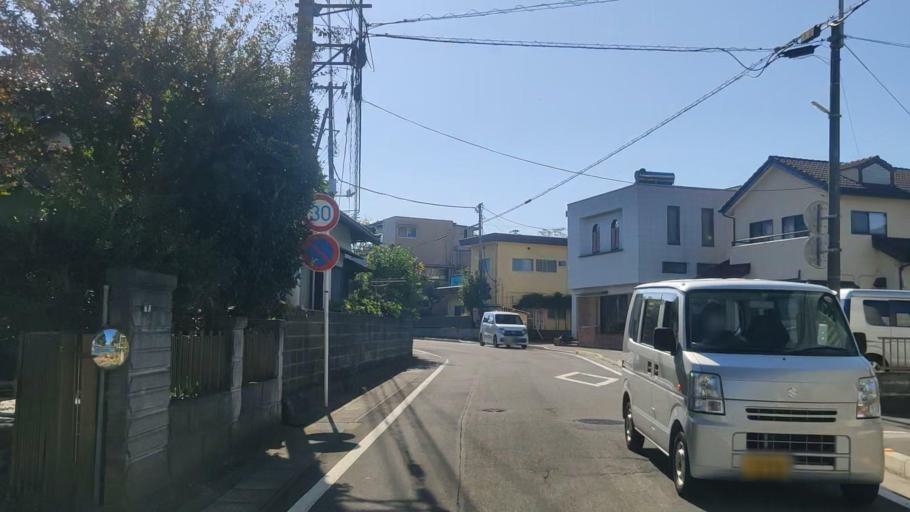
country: JP
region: Shizuoka
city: Mishima
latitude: 35.0128
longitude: 138.9459
